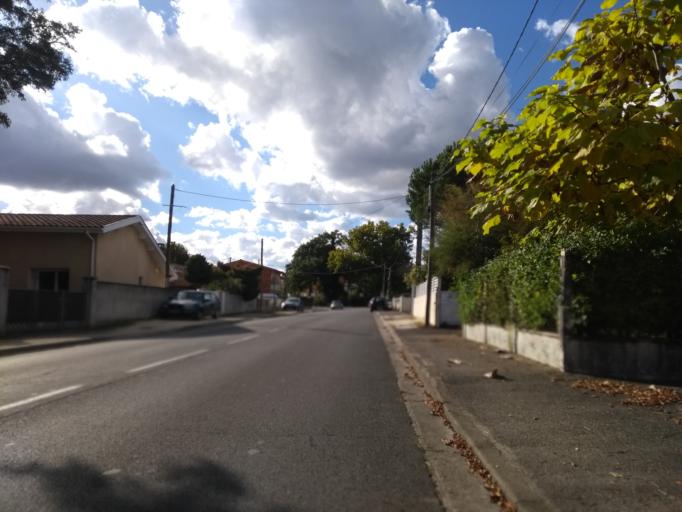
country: FR
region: Aquitaine
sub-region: Departement de la Gironde
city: Canejan
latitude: 44.7635
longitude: -0.6248
